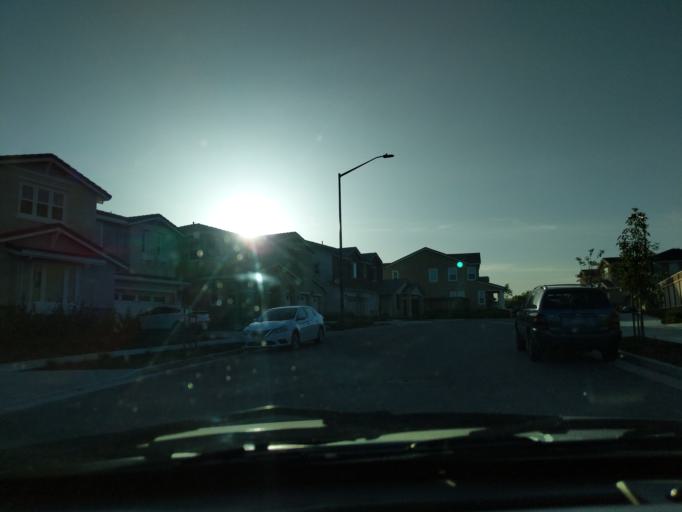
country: US
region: California
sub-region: Santa Clara County
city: Gilroy
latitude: 36.9914
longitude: -121.5822
